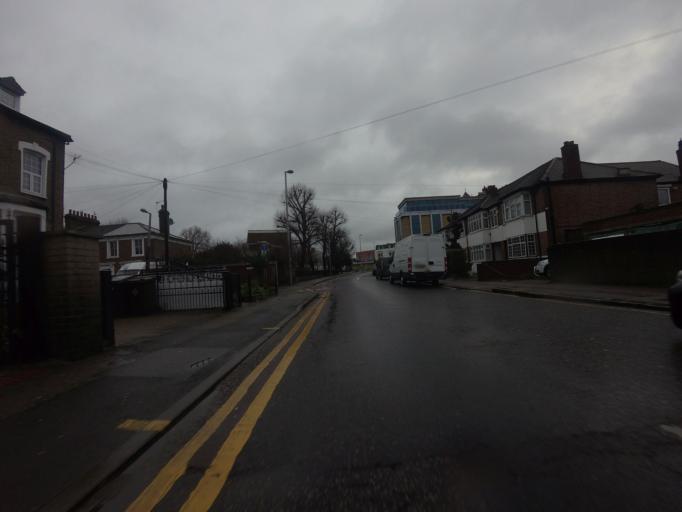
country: GB
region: England
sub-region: Greater London
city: Walthamstow
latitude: 51.5643
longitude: -0.0123
